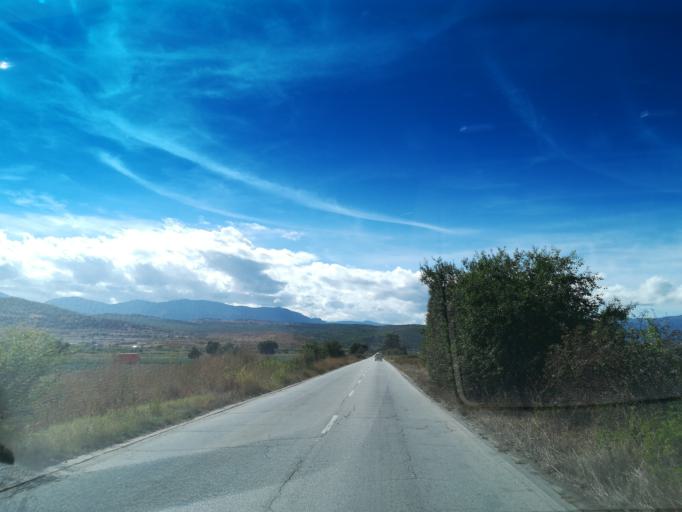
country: BG
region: Plovdiv
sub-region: Obshtina Krichim
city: Krichim
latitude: 42.0800
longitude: 24.4187
